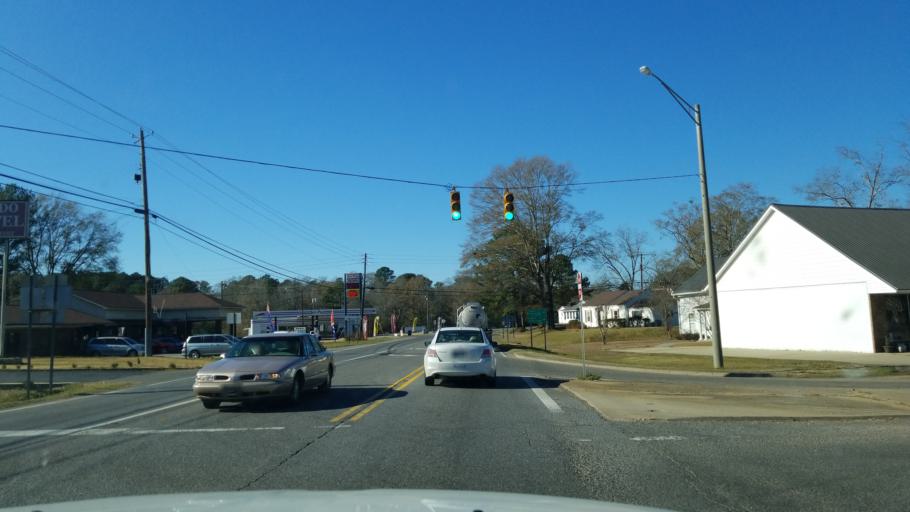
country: US
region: Alabama
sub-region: Pickens County
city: Gordo
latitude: 33.3164
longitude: -87.9031
